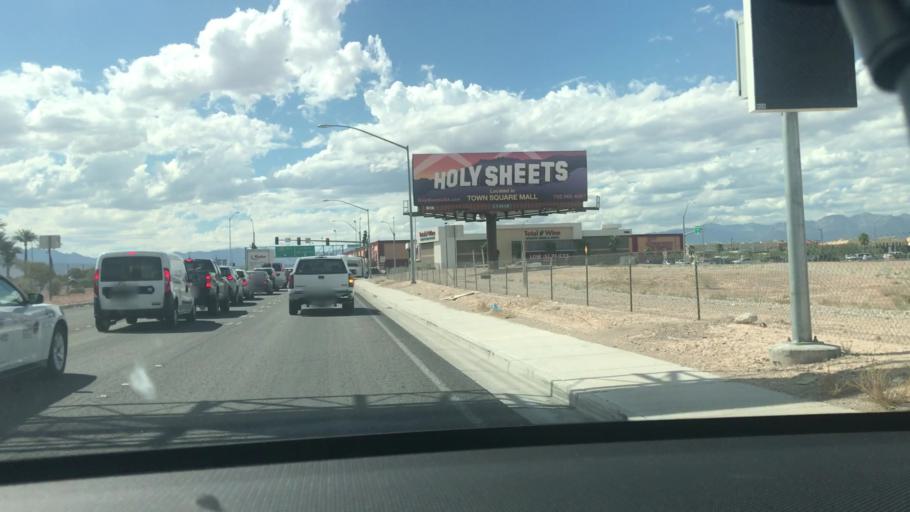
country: US
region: Nevada
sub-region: Clark County
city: Paradise
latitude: 36.0645
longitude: -115.1708
